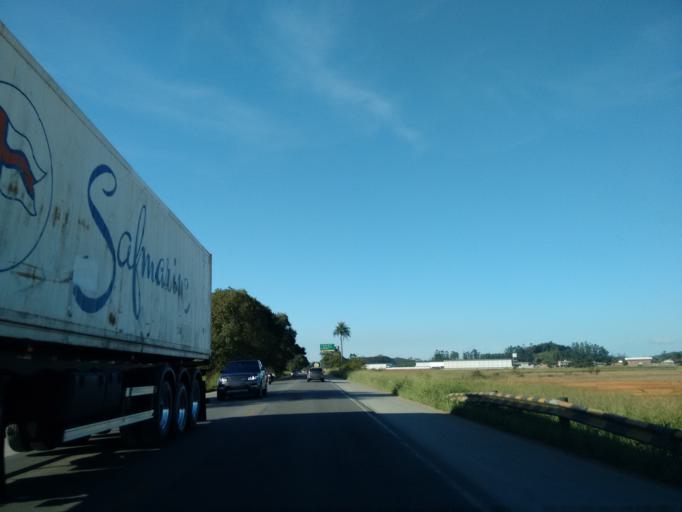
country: BR
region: Santa Catarina
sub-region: Guaramirim
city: Guaramirim
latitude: -26.4697
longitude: -48.9670
